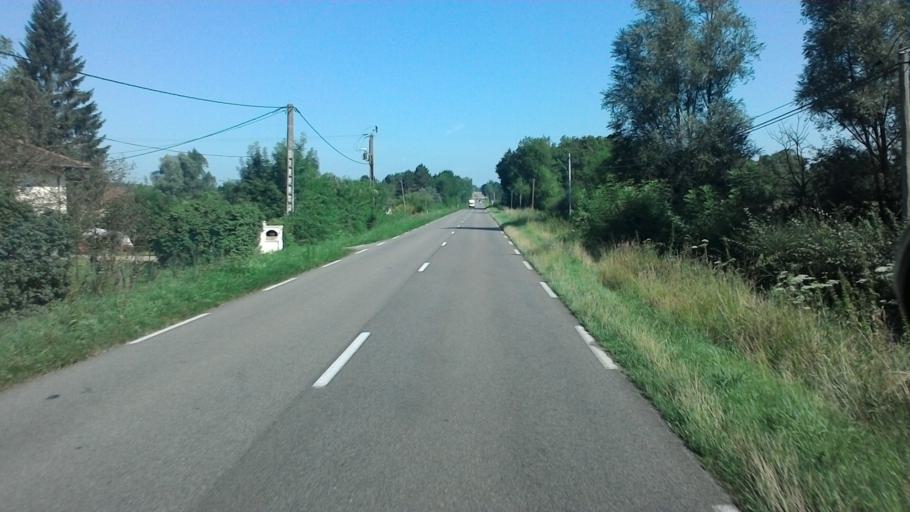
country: FR
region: Rhone-Alpes
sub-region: Departement de l'Ain
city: Saint-Trivier-de-Courtes
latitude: 46.4156
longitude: 5.1030
